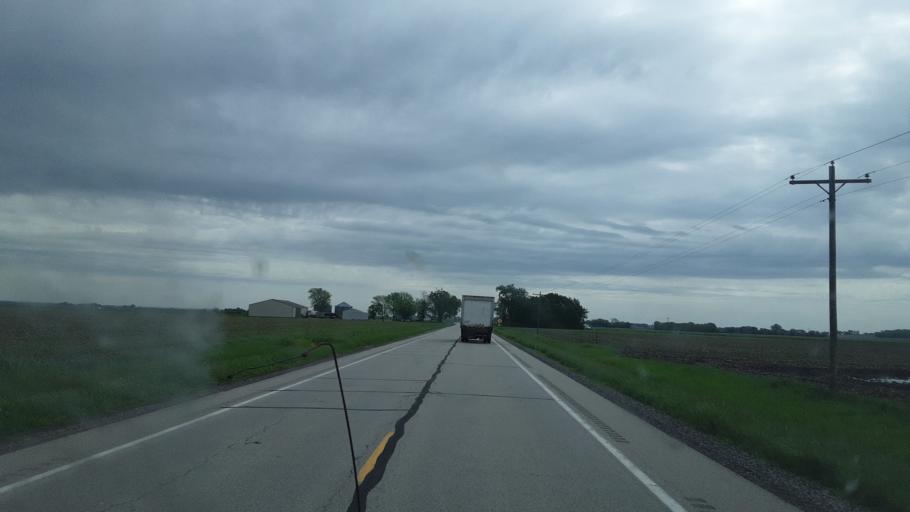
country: US
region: Illinois
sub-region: Mason County
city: Mason City
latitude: 40.3047
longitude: -89.7026
